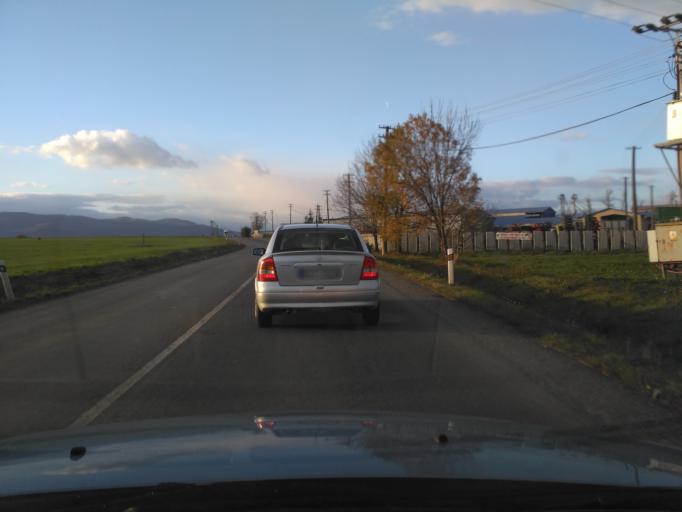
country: SK
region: Kosicky
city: Secovce
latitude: 48.6550
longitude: 21.6727
